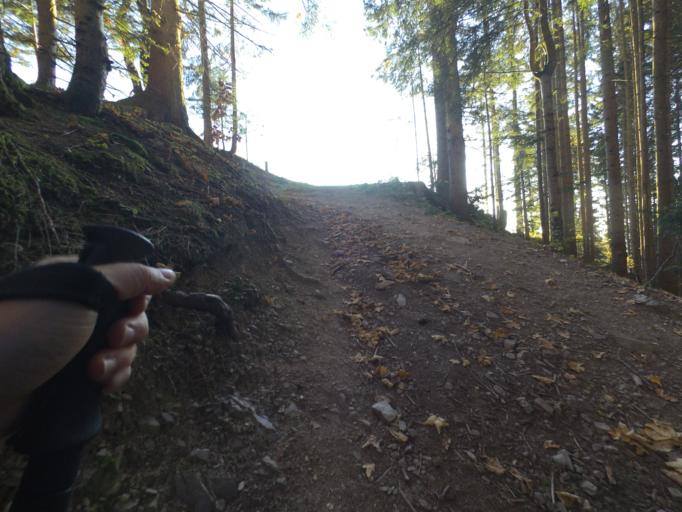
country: AT
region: Salzburg
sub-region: Politischer Bezirk Sankt Johann im Pongau
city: Pfarrwerfen
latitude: 47.4781
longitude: 13.2170
